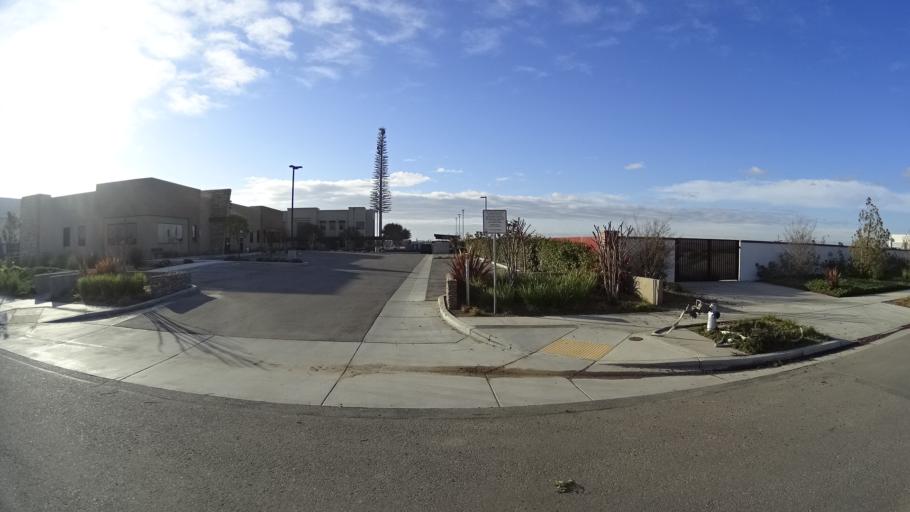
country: US
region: California
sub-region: Kern County
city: Rosedale
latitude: 35.3128
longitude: -119.1325
